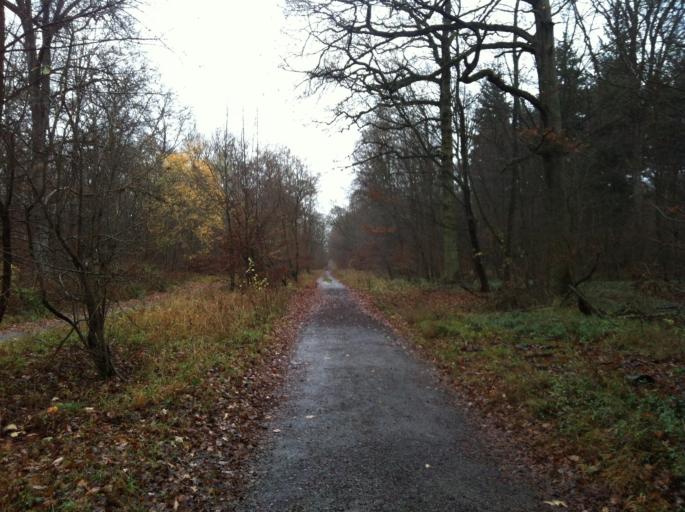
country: DE
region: Rheinland-Pfalz
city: Ober-Olm
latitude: 49.9615
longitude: 8.1710
